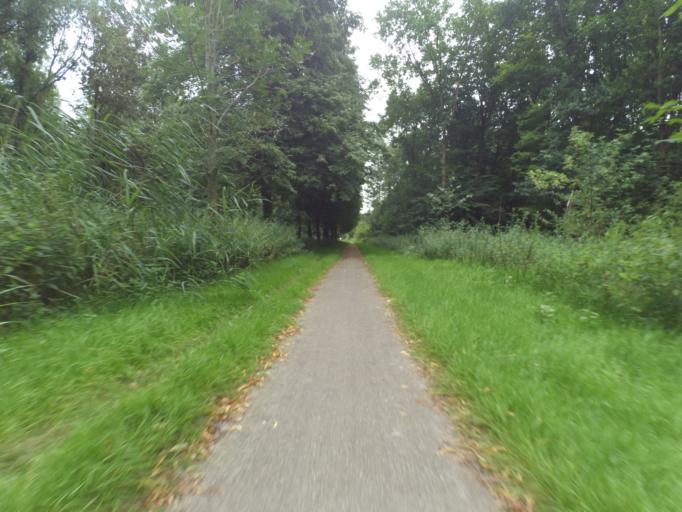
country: NL
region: Flevoland
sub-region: Gemeente Lelystad
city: Lelystad
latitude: 52.4563
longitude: 5.4352
